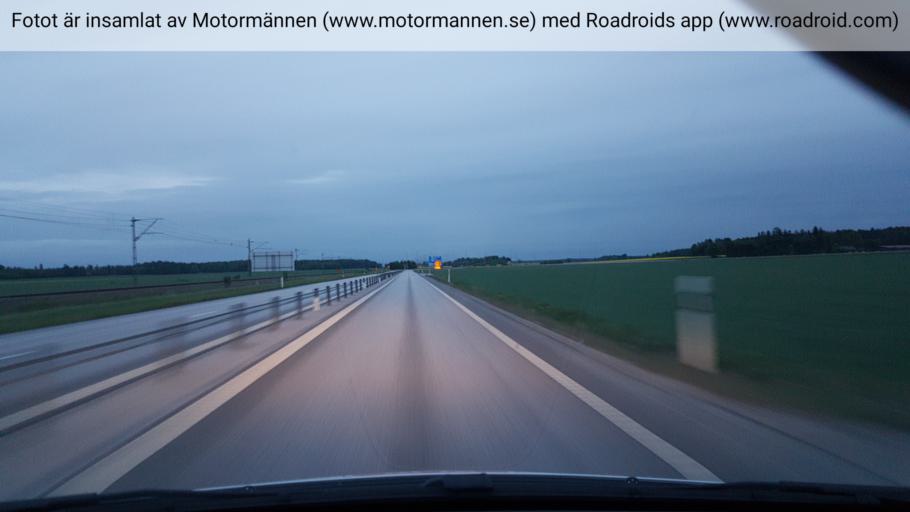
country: SE
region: Vaestmanland
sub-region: Sala Kommun
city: Sala
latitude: 59.8927
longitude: 16.6228
